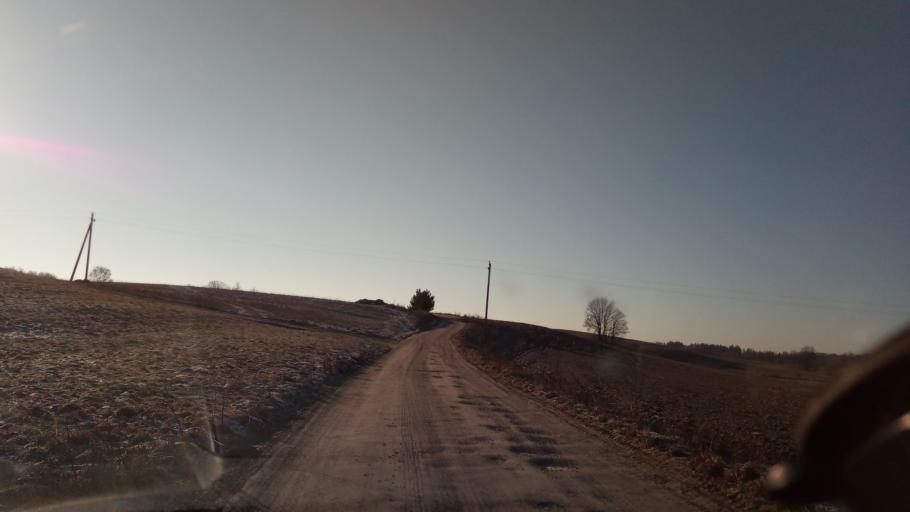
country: LT
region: Alytaus apskritis
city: Druskininkai
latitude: 54.1129
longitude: 24.0137
